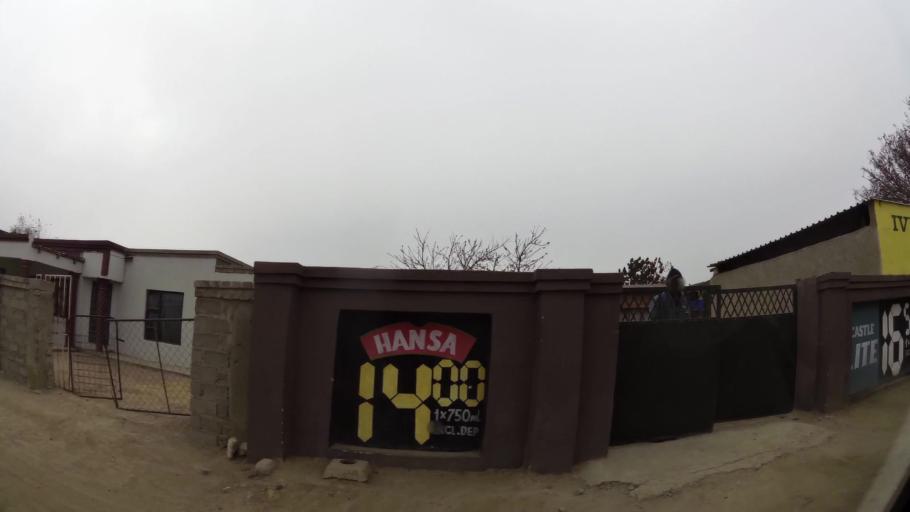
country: ZA
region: Limpopo
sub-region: Capricorn District Municipality
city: Polokwane
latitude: -23.8478
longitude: 29.3977
